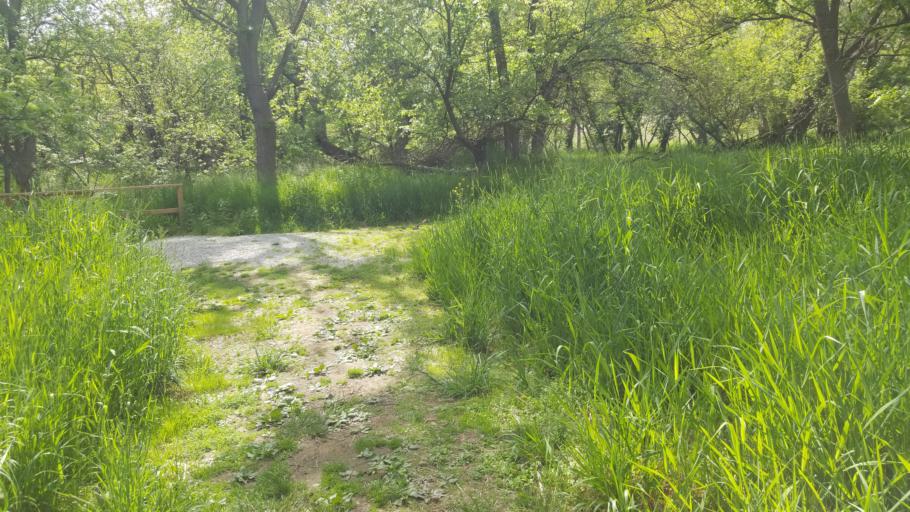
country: US
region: Nebraska
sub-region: Sarpy County
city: Chalco
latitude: 41.1713
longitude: -96.1650
